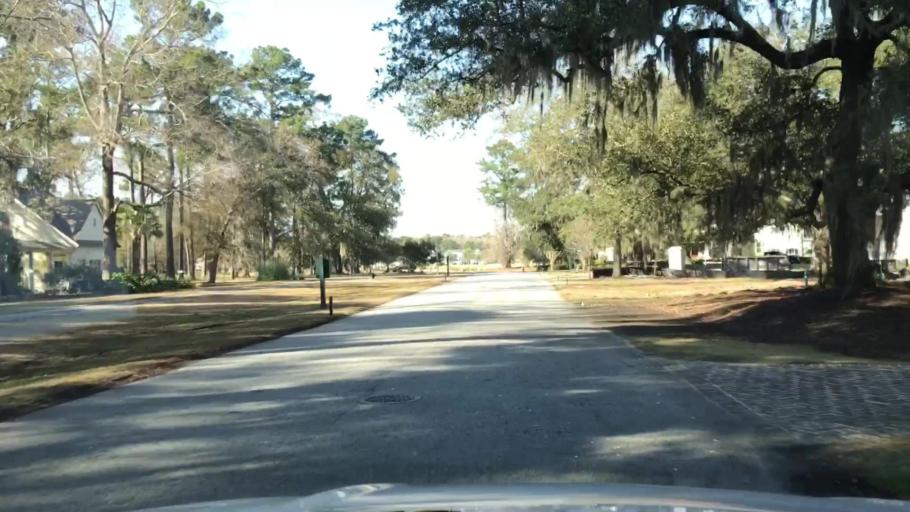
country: US
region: South Carolina
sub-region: Beaufort County
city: Bluffton
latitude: 32.3391
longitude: -80.9112
